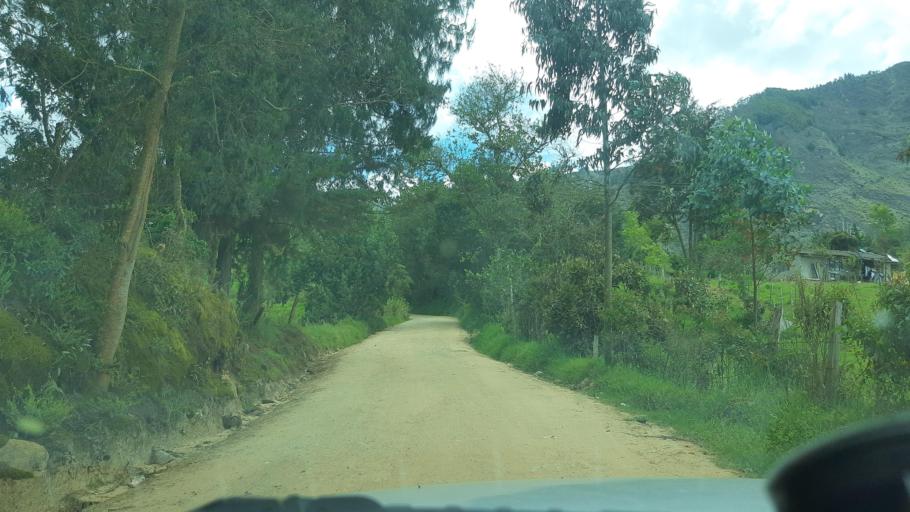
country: CO
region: Cundinamarca
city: Umbita
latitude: 5.2205
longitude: -73.4482
